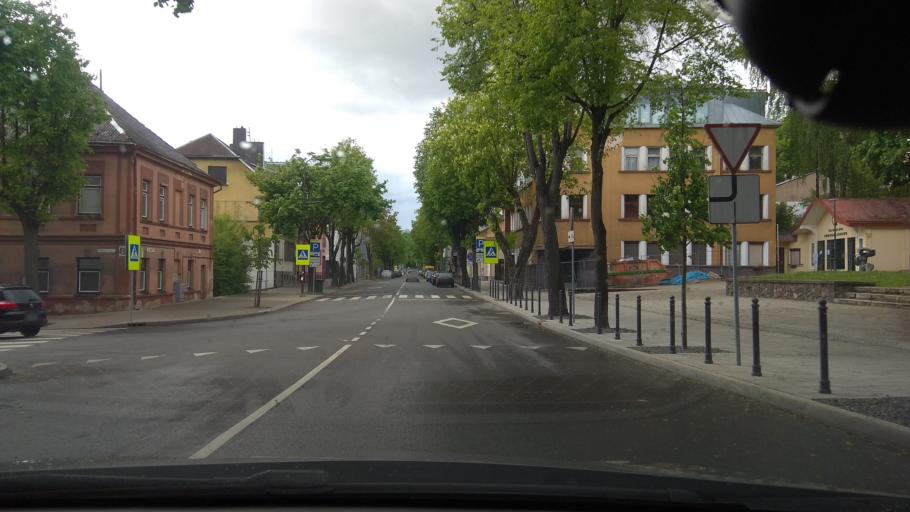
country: LT
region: Kauno apskritis
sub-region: Kaunas
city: Kaunas
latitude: 54.9005
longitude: 23.9183
